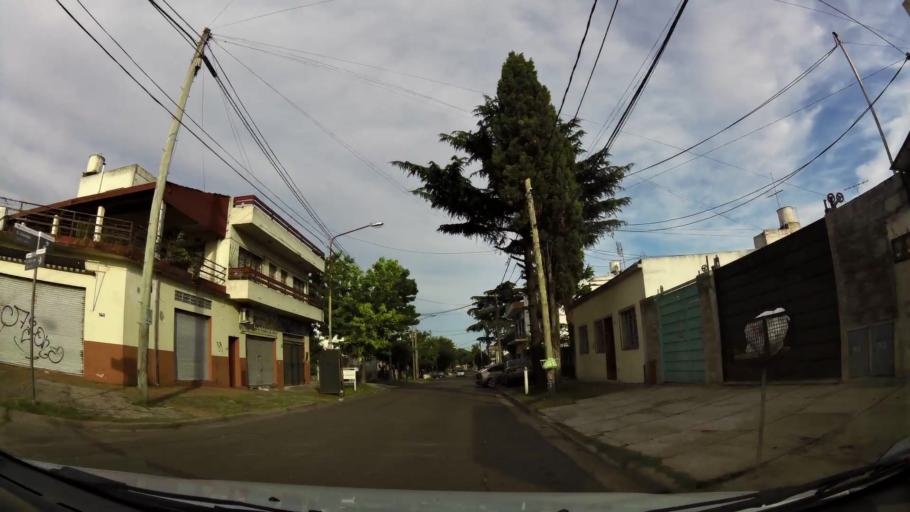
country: AR
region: Buenos Aires
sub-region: Partido de Moron
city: Moron
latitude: -34.6392
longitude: -58.6280
